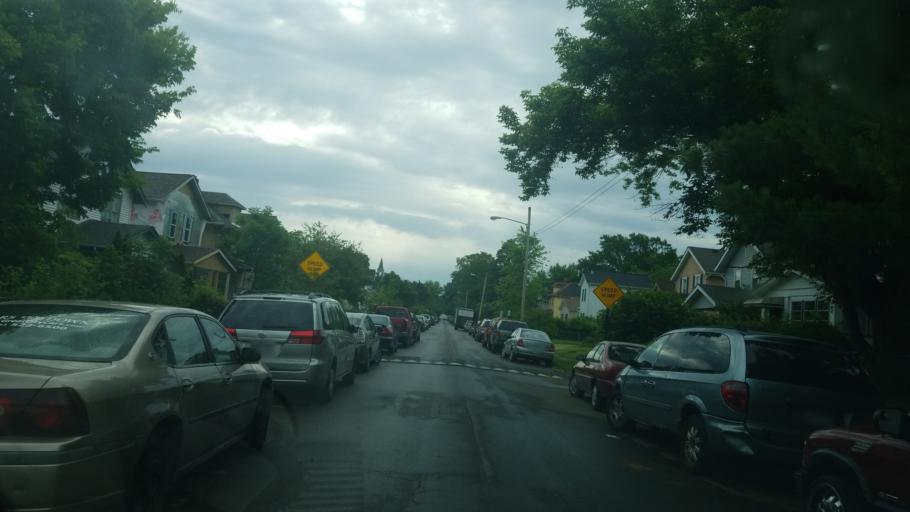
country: US
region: Ohio
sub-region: Franklin County
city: Bexley
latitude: 40.0200
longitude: -82.9711
